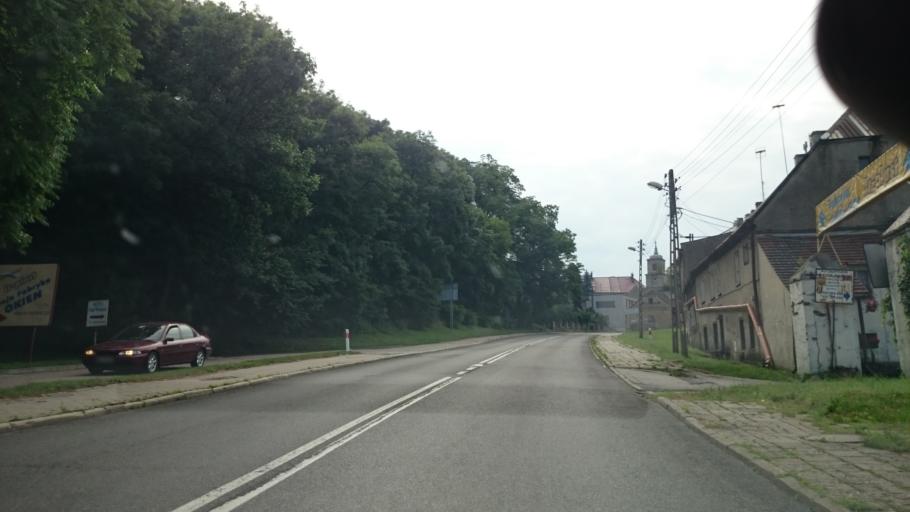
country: PL
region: Silesian Voivodeship
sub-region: Powiat gliwicki
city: Toszek
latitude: 50.4553
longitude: 18.5138
